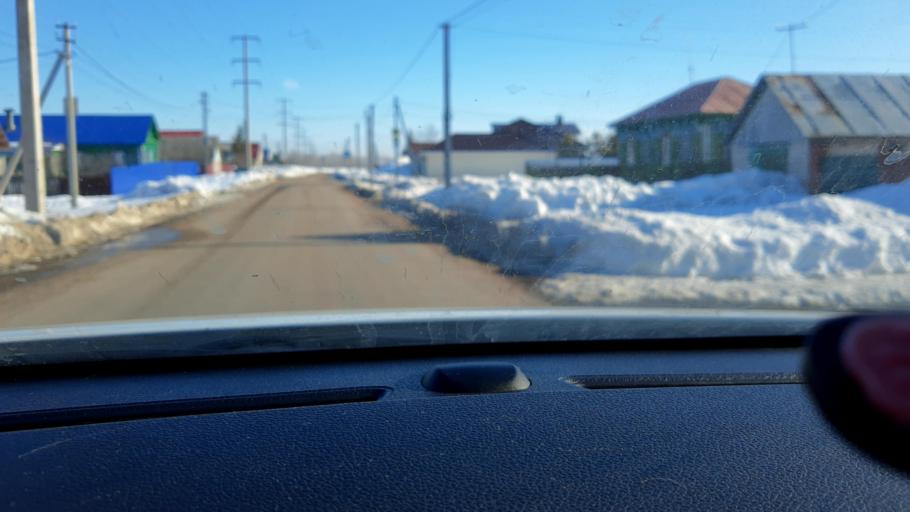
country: RU
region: Bashkortostan
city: Kabakovo
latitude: 54.5211
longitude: 55.9482
